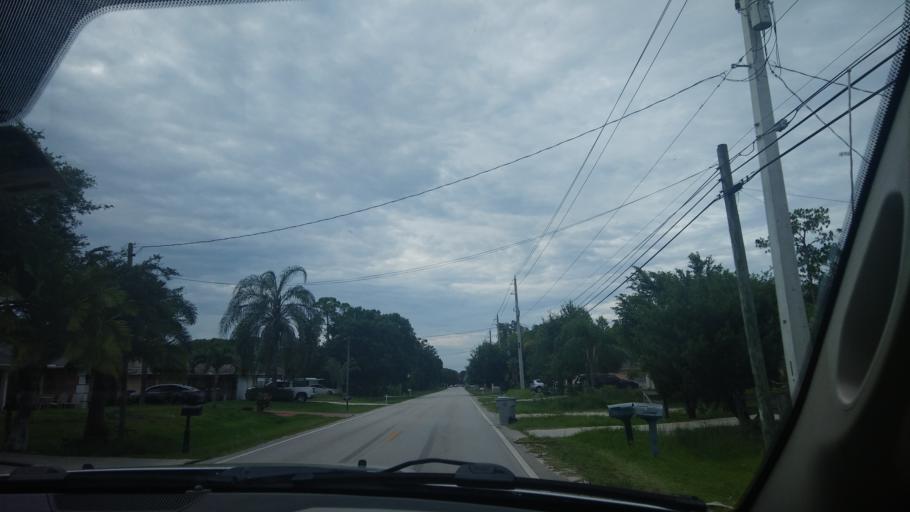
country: US
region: Florida
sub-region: Indian River County
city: Fellsmere
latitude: 27.7631
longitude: -80.5932
